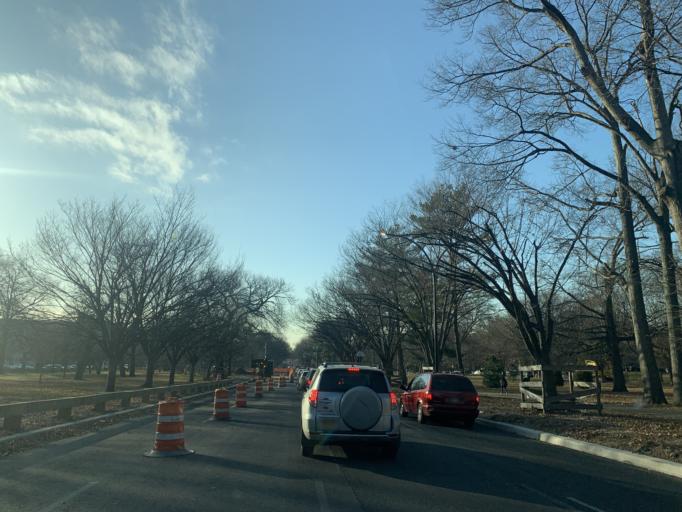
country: US
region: New York
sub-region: Bronx
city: The Bronx
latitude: 40.8575
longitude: -73.8598
